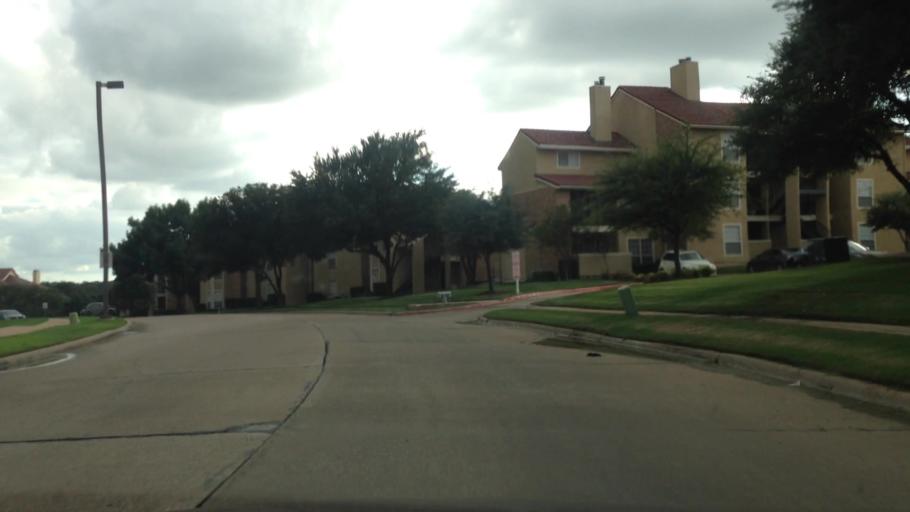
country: US
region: Texas
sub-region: Dallas County
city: Irving
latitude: 32.8827
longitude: -96.9662
